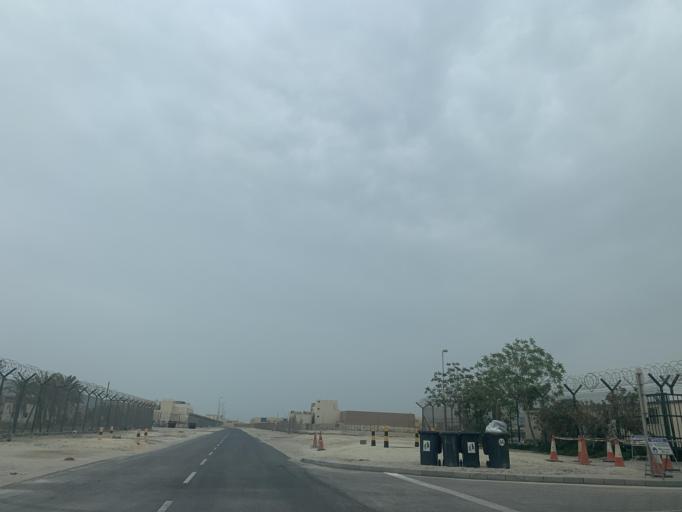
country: BH
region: Muharraq
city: Al Hadd
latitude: 26.2192
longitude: 50.6603
